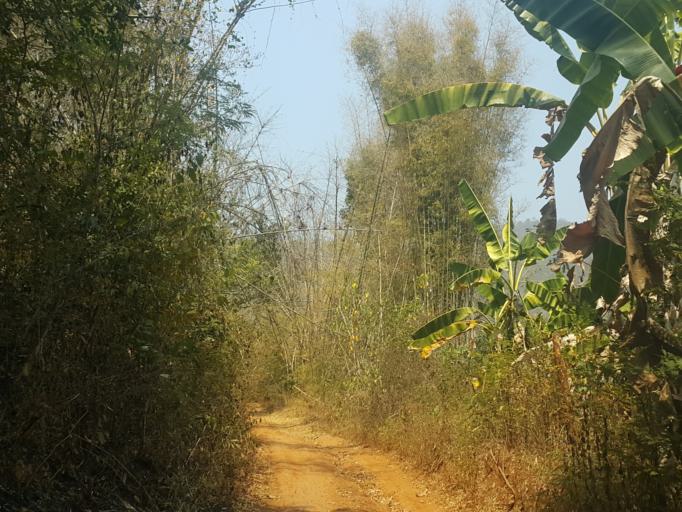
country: TH
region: Chiang Mai
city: Hang Dong
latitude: 18.7544
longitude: 98.8276
